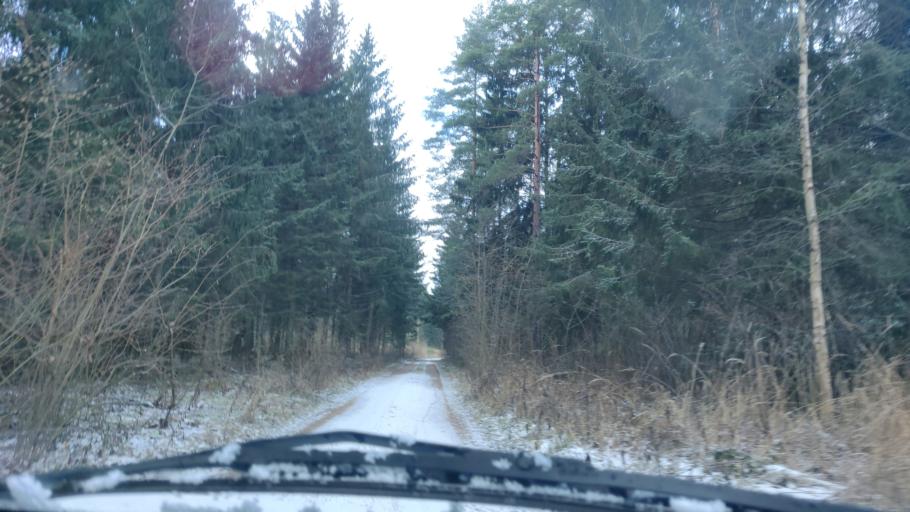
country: LT
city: Trakai
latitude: 54.5814
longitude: 24.9656
